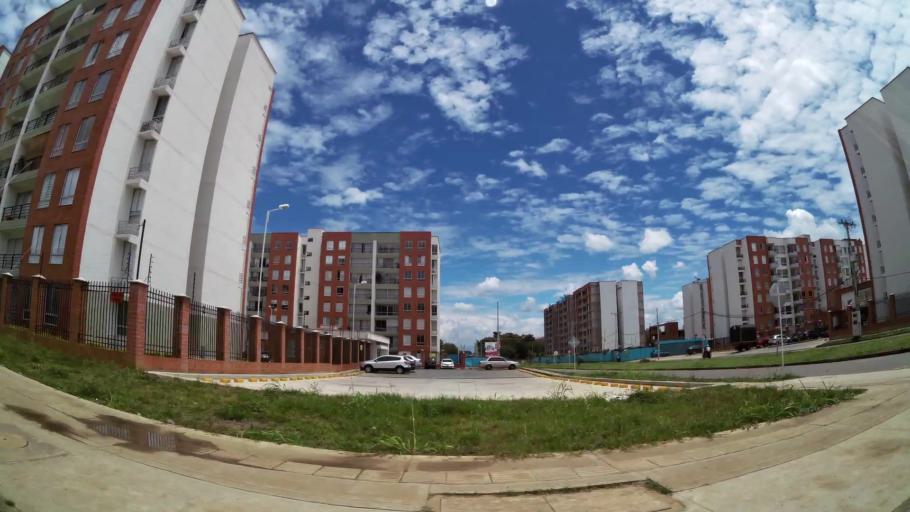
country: CO
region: Valle del Cauca
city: Cali
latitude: 3.3710
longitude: -76.5162
